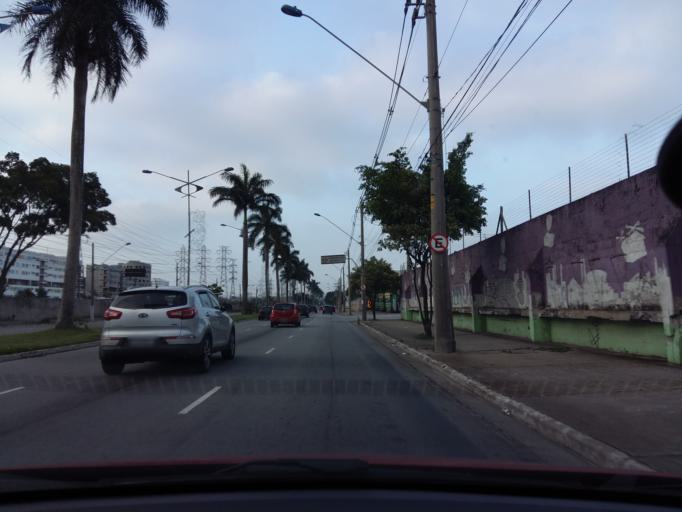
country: BR
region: Sao Paulo
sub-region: Sao Caetano Do Sul
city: Sao Caetano do Sul
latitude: -23.6205
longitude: -46.5815
